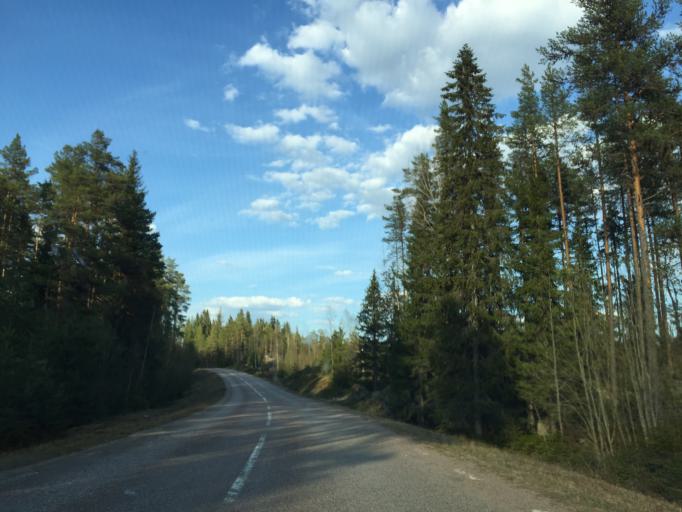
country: SE
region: Dalarna
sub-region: Vansbro Kommun
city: Jarna
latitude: 60.6033
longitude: 14.5199
